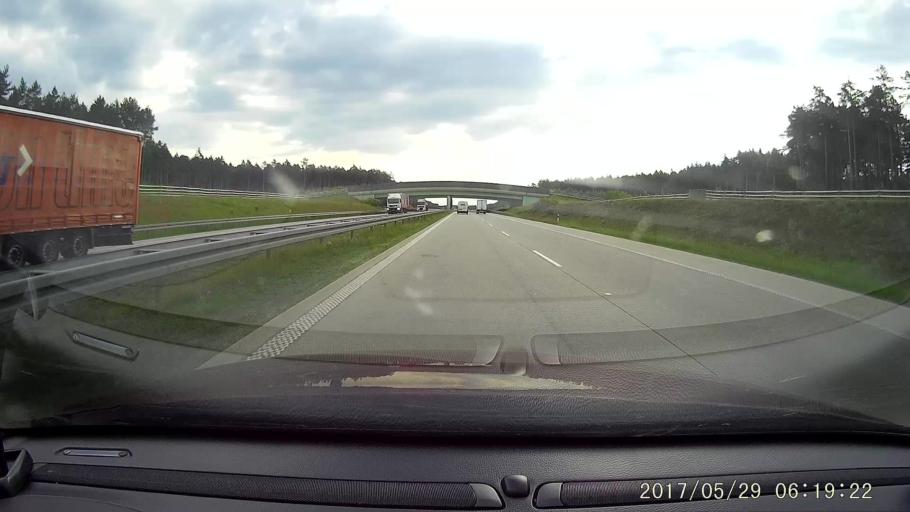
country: PL
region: Lower Silesian Voivodeship
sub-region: Powiat boleslawiecki
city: Nowogrodziec
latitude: 51.2796
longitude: 15.4622
